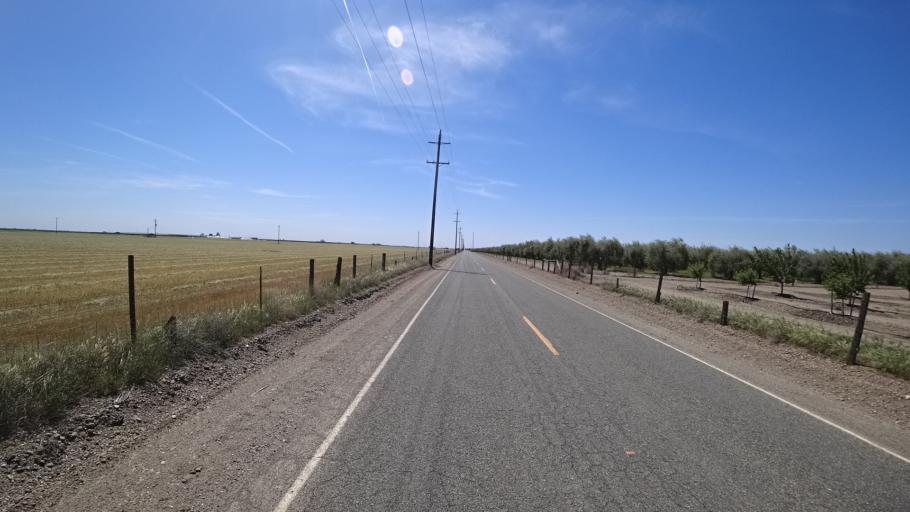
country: US
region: California
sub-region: Glenn County
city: Orland
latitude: 39.6639
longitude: -122.1783
